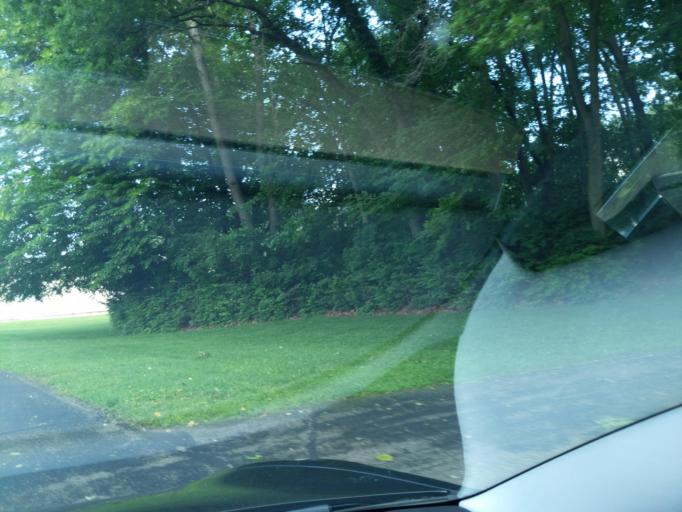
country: US
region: Michigan
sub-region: Jackson County
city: Jackson
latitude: 42.2291
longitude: -84.3710
